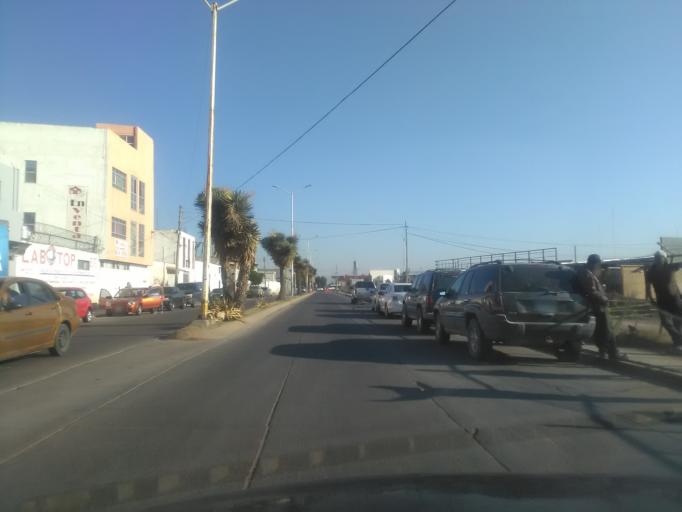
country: MX
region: Durango
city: Victoria de Durango
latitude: 24.0446
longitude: -104.6226
